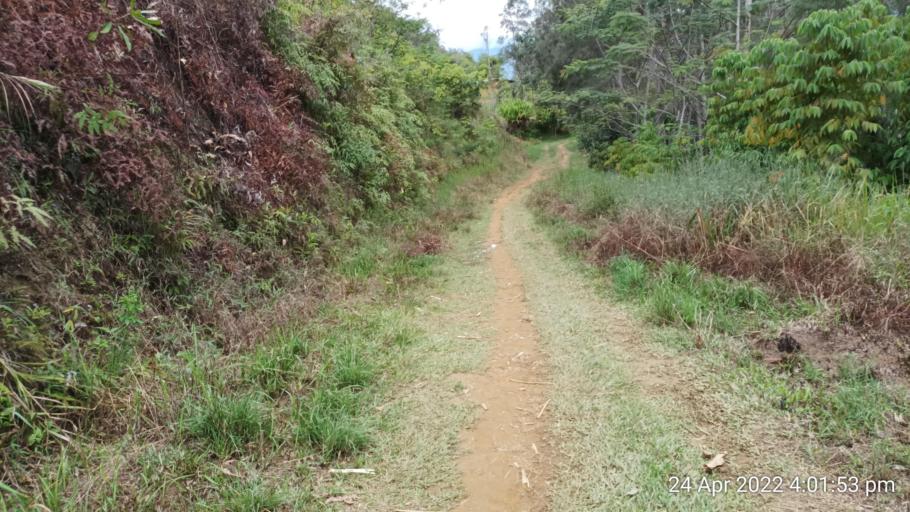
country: PG
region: Jiwaka
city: Minj
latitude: -5.9006
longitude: 144.8231
